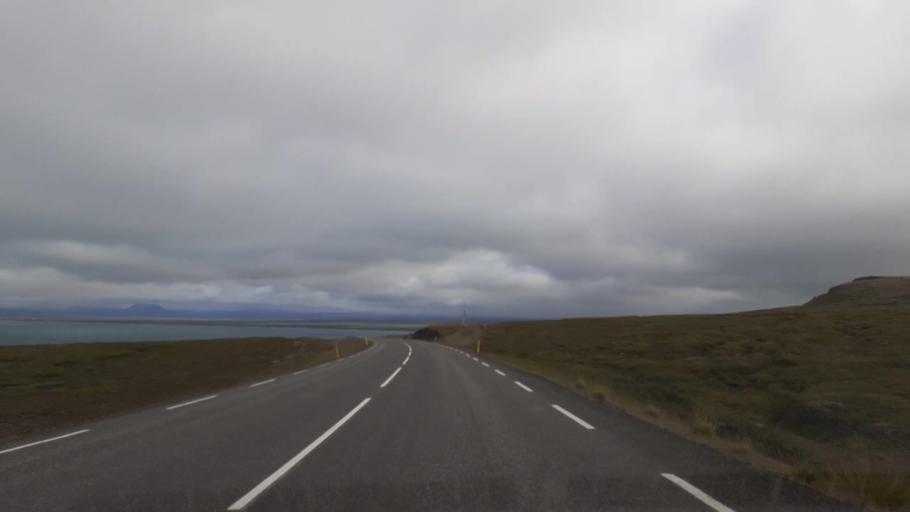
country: IS
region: Northeast
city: Husavik
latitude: 66.1497
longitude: -16.9778
